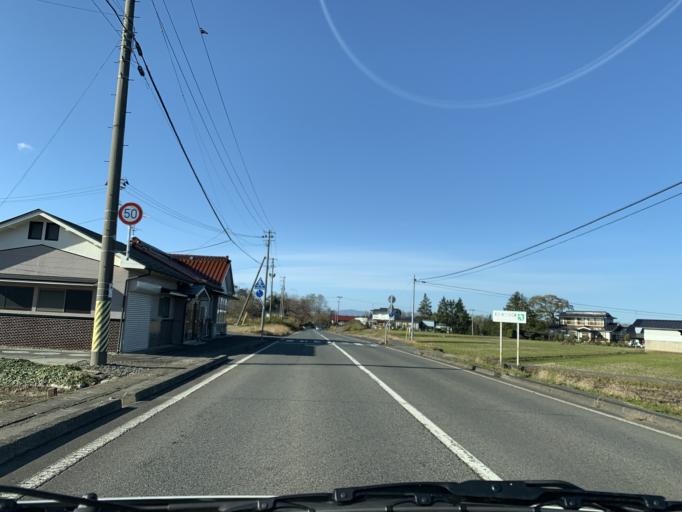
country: JP
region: Iwate
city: Mizusawa
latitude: 39.1824
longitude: 141.1305
